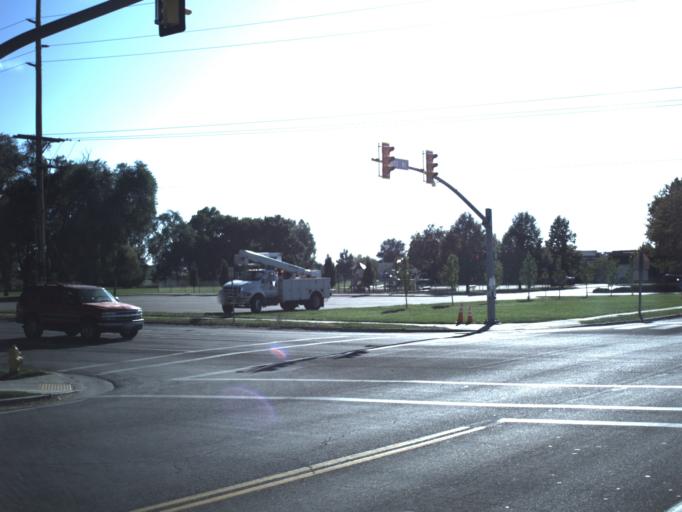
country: US
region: Utah
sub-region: Davis County
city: Clinton
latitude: 41.1399
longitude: -112.0450
